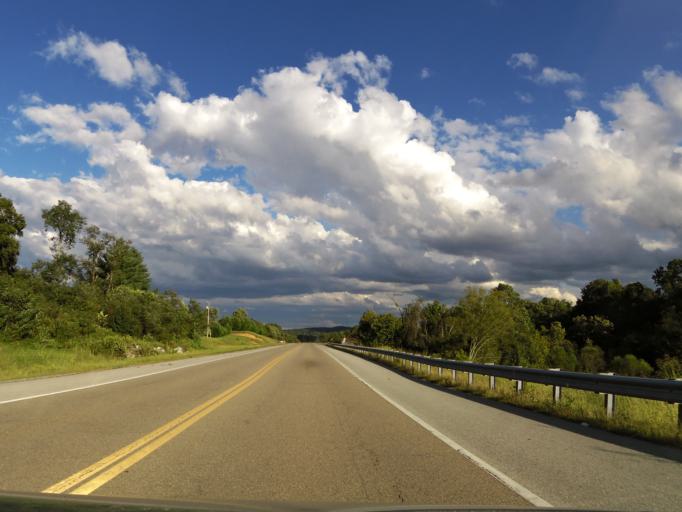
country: US
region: Tennessee
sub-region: Grainger County
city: Blaine
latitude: 36.1601
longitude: -83.7312
